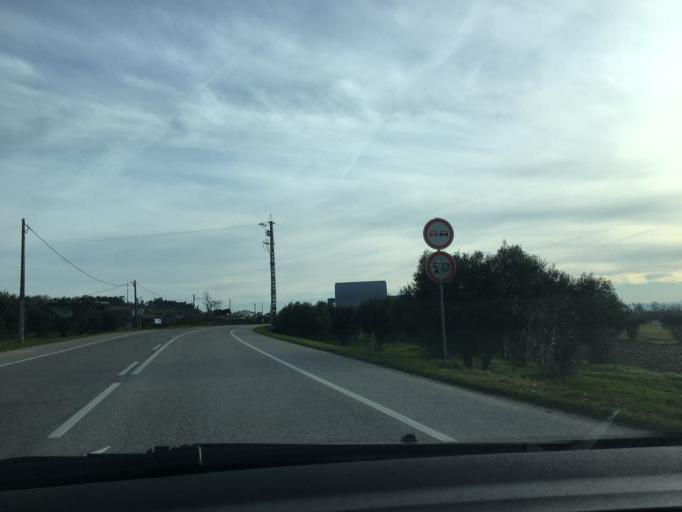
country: PT
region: Coimbra
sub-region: Soure
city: Alfarelos
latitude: 40.2054
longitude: -8.6320
